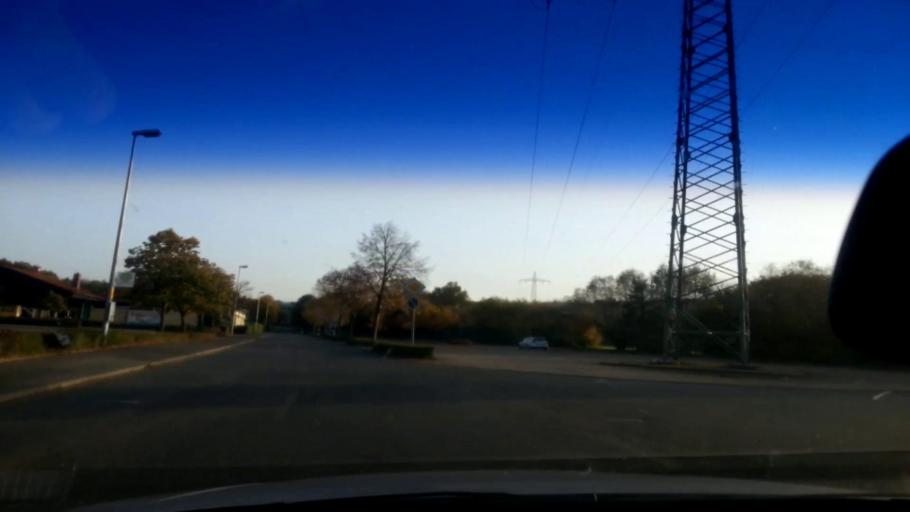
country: DE
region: Bavaria
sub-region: Upper Franconia
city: Zapfendorf
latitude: 50.0122
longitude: 10.9331
